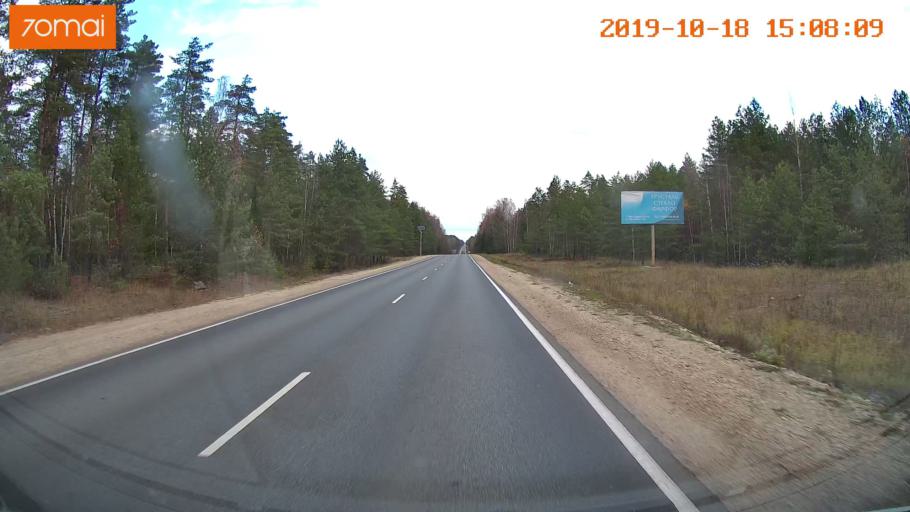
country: RU
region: Vladimir
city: Gus'-Khrustal'nyy
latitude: 55.5485
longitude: 40.6076
